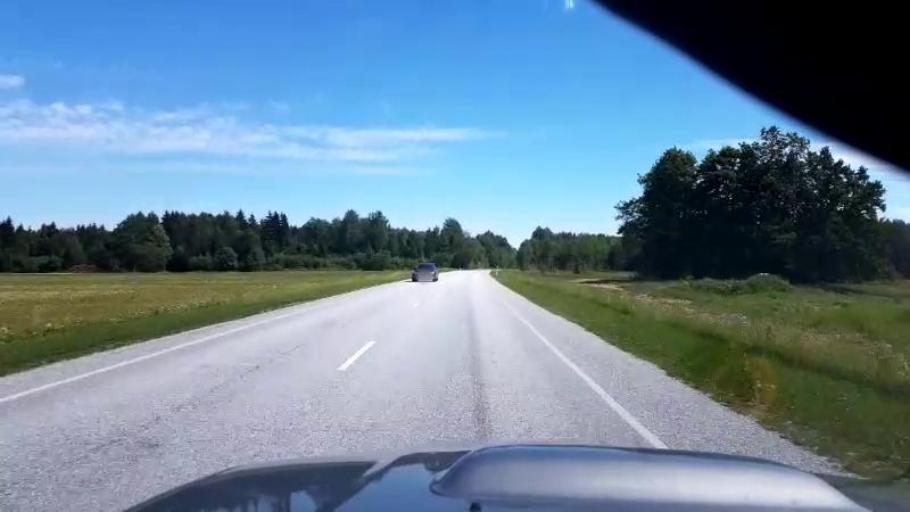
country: EE
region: Laeaene-Virumaa
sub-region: Rakke vald
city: Rakke
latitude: 58.9623
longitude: 26.1582
